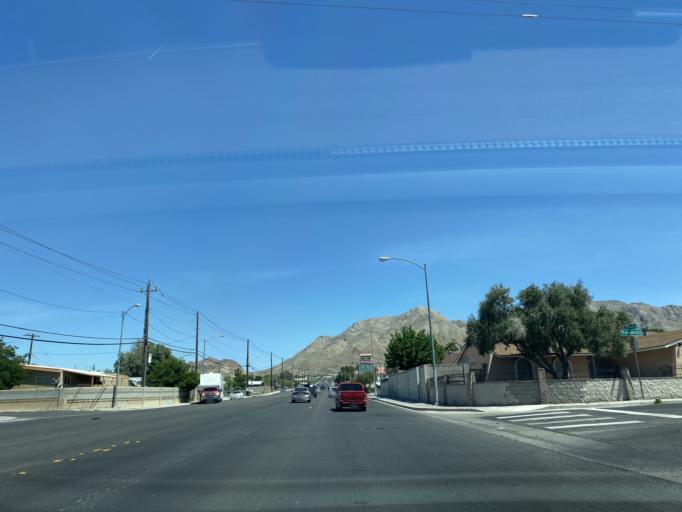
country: US
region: Nevada
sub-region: Clark County
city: Sunrise Manor
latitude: 36.1961
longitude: -115.0427
